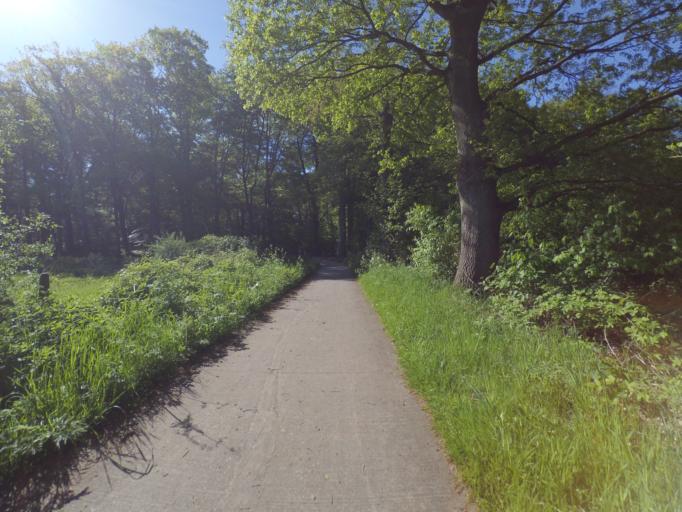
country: NL
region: Gelderland
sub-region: Gemeente Rheden
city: Spankeren
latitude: 52.1066
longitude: 6.1095
